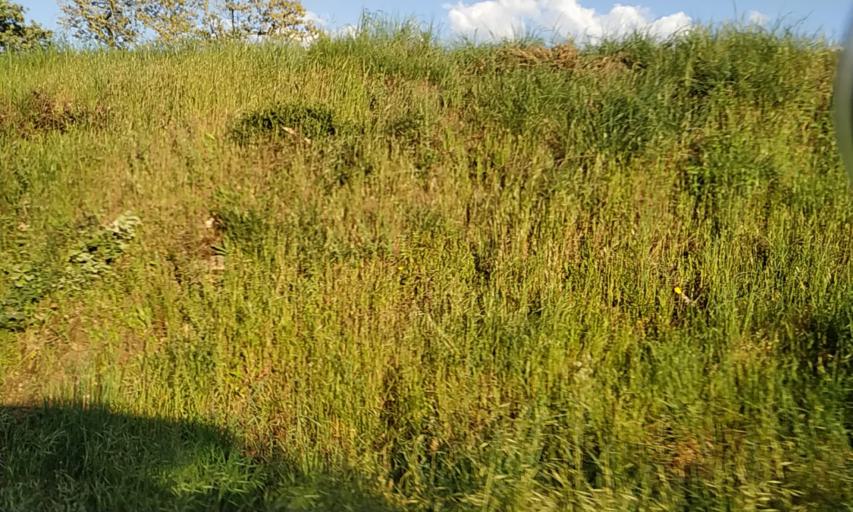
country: PT
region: Portalegre
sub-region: Marvao
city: Marvao
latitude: 39.3644
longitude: -7.3949
